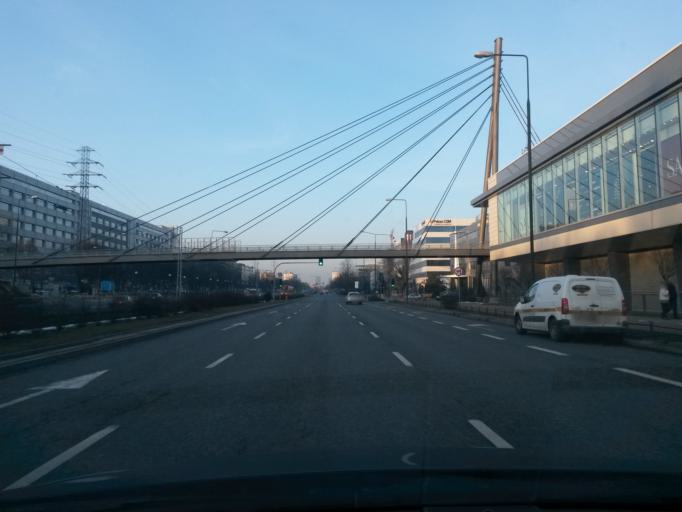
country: PL
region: Masovian Voivodeship
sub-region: Warszawa
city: Mokotow
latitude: 52.1801
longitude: 21.0025
